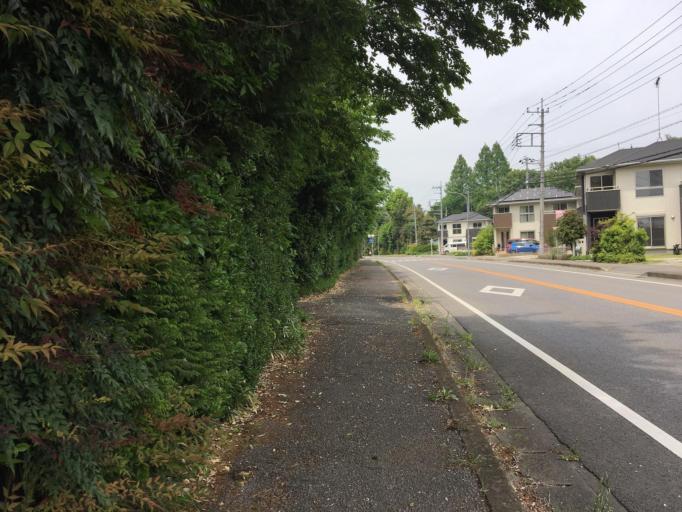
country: JP
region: Tochigi
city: Oyama
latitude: 36.3411
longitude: 139.8166
